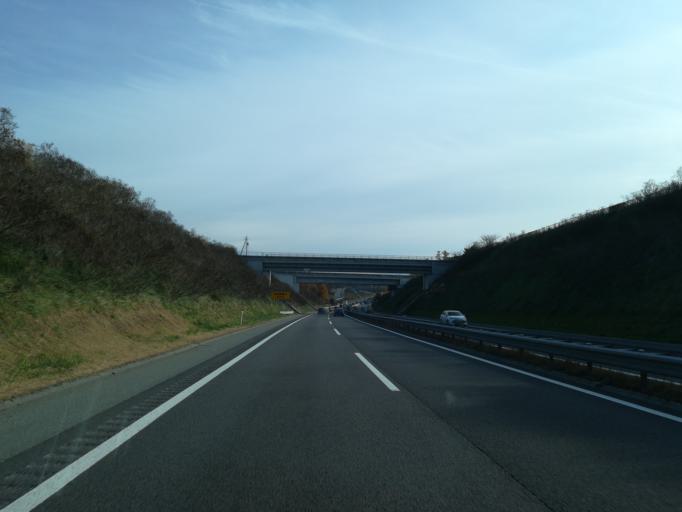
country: JP
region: Nagano
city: Komoro
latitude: 36.3200
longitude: 138.4766
